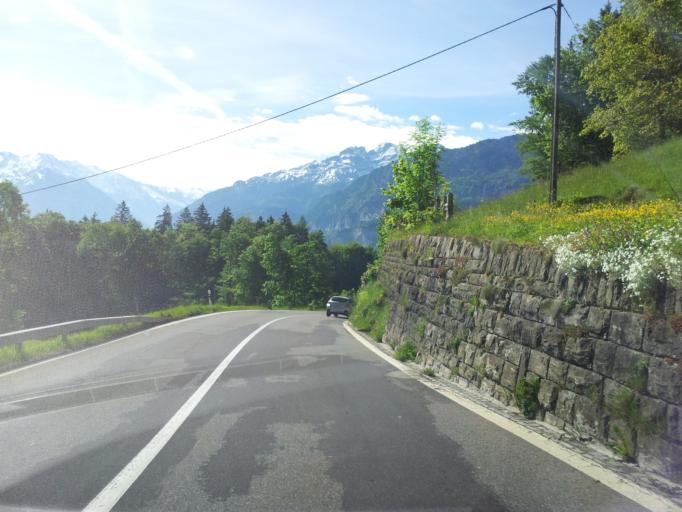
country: CH
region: Obwalden
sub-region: Obwalden
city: Lungern
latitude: 46.7529
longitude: 8.1271
